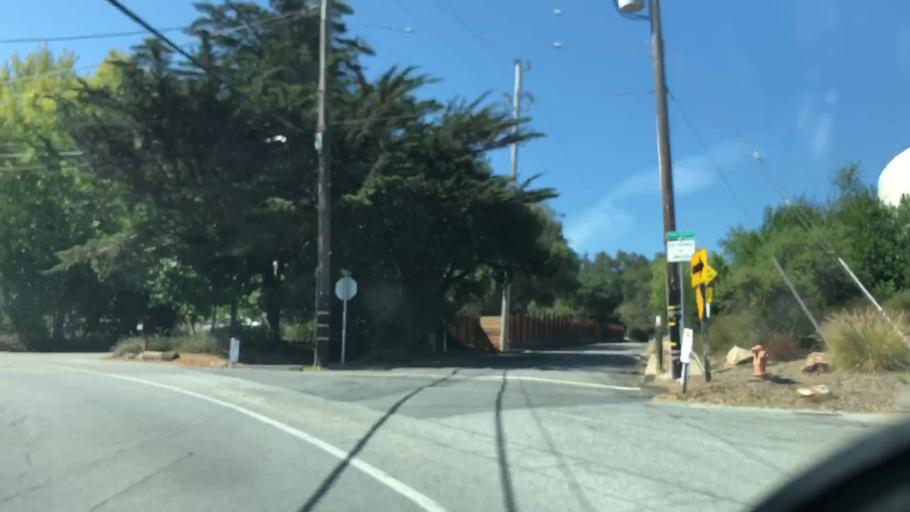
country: US
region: California
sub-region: Santa Cruz County
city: Corralitos
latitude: 36.9944
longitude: -121.8159
